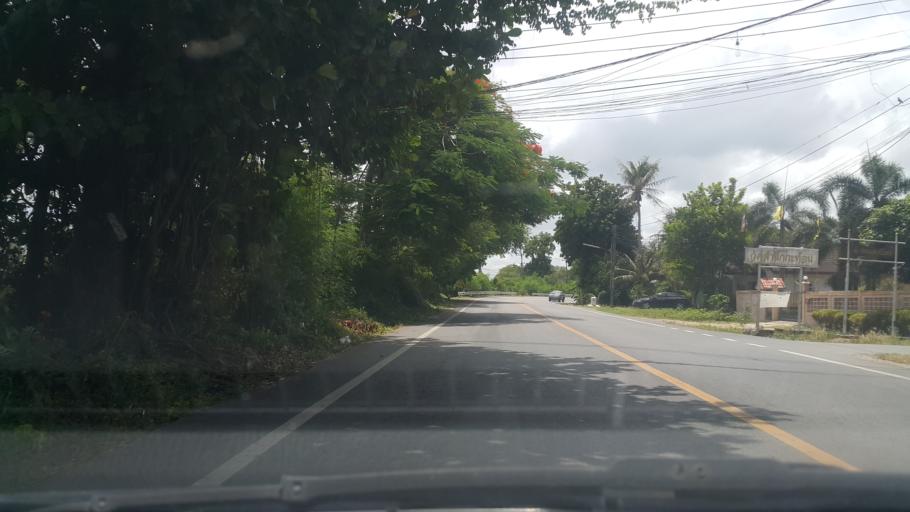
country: TH
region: Rayong
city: Ban Chang
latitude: 12.7714
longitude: 101.0201
